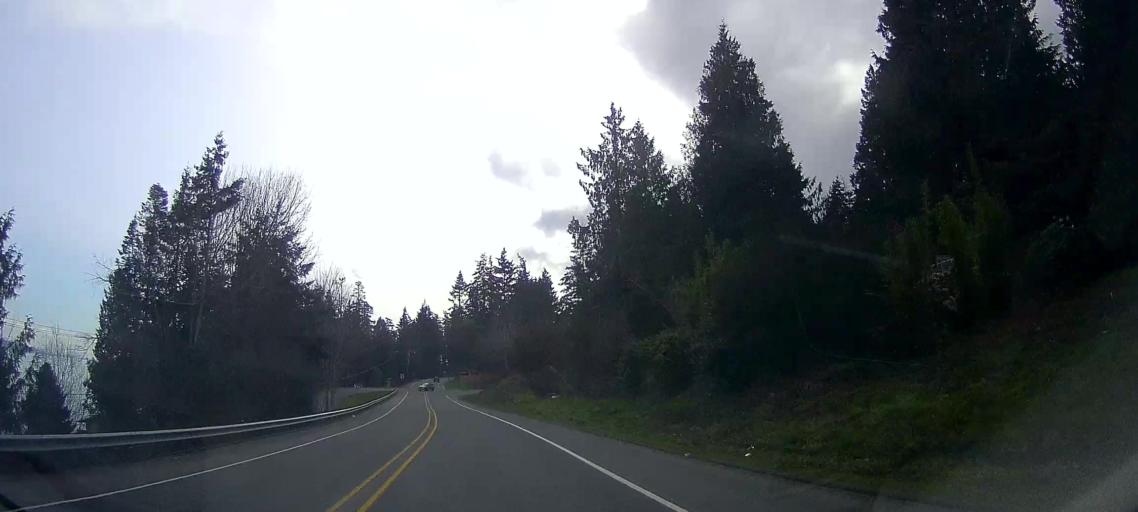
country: US
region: Washington
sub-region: Island County
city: Camano
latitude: 48.1837
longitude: -122.4807
